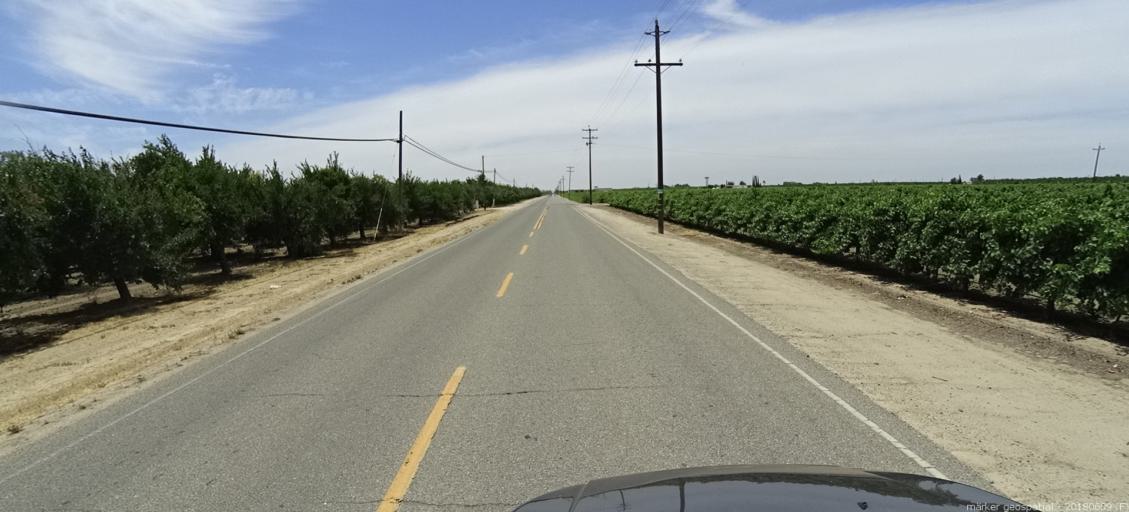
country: US
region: California
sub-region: Madera County
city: Parkwood
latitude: 36.9094
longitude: -120.0639
